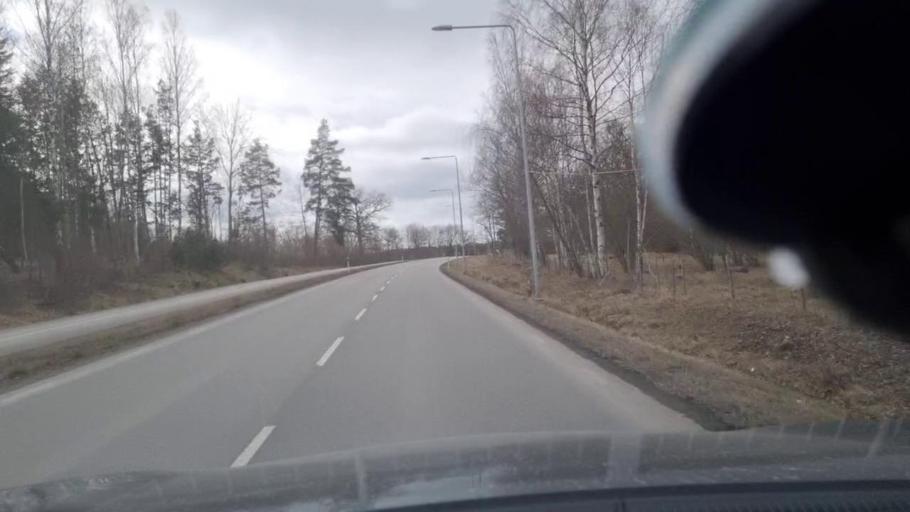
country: SE
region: Stockholm
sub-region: Jarfalla Kommun
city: Jakobsberg
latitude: 59.4256
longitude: 17.7898
